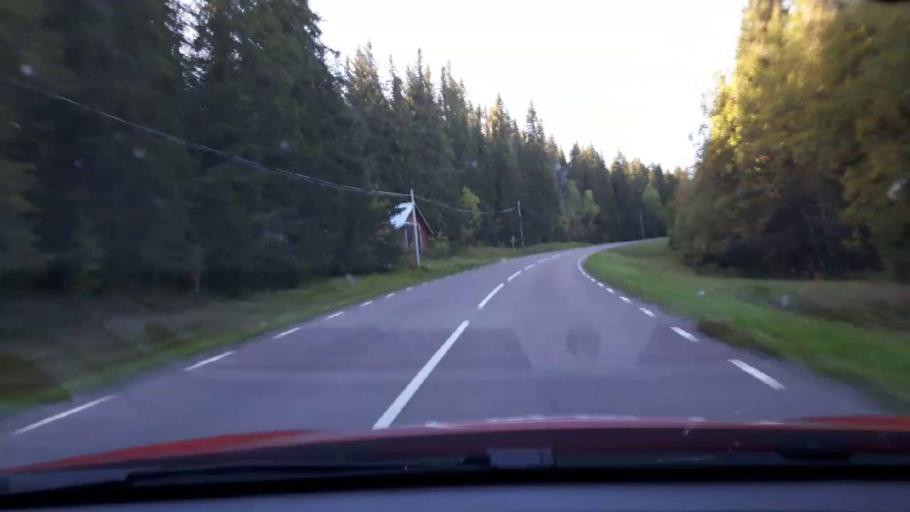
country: SE
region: Jaemtland
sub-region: Stroemsunds Kommun
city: Stroemsund
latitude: 63.8409
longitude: 15.3539
